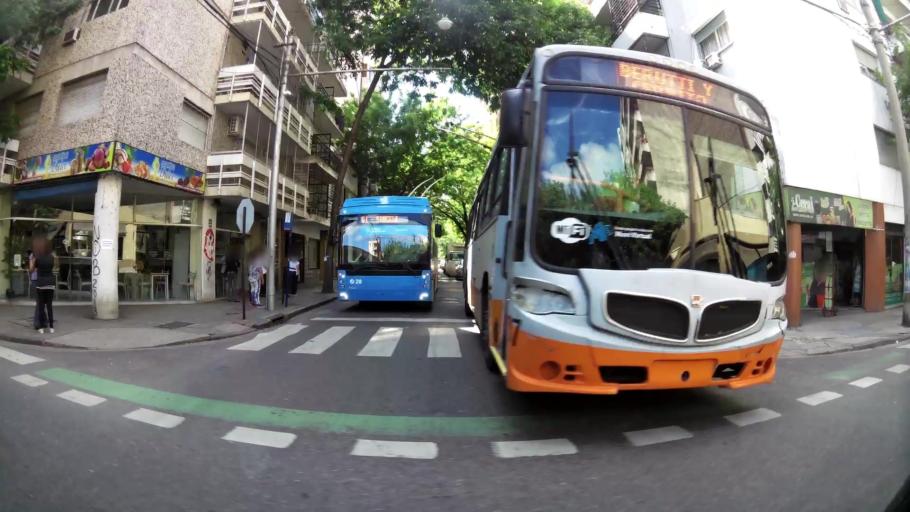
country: AR
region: Santa Fe
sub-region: Departamento de Rosario
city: Rosario
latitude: -32.9545
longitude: -60.6299
